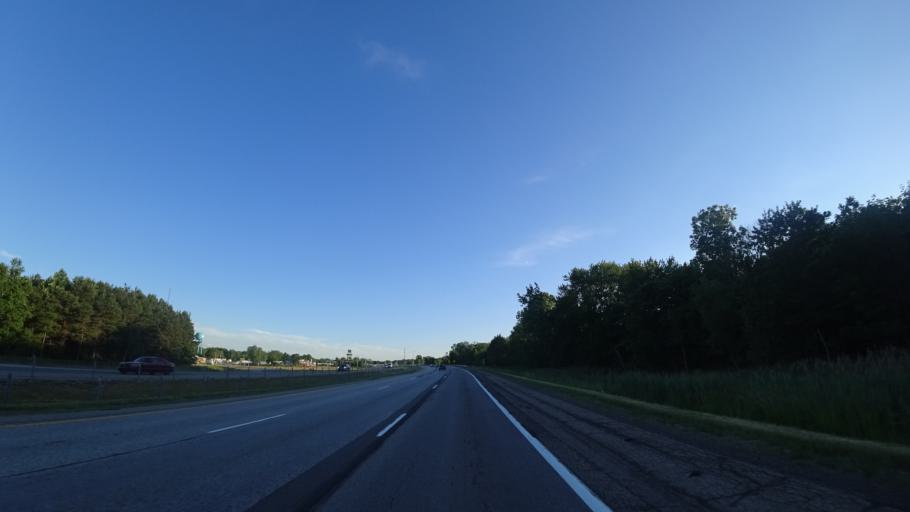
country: US
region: Michigan
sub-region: Berrien County
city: Shorewood-Tower Hills-Harbert
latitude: 41.8893
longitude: -86.5990
